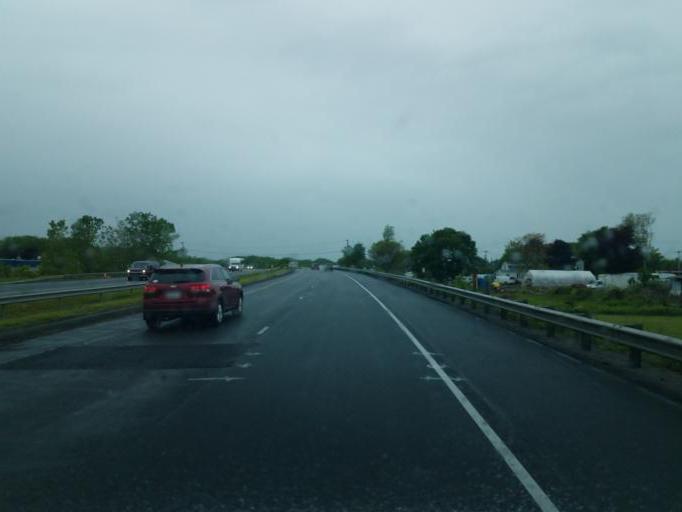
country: US
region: New York
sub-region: Oneida County
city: Whitesboro
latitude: 43.1372
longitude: -75.2738
